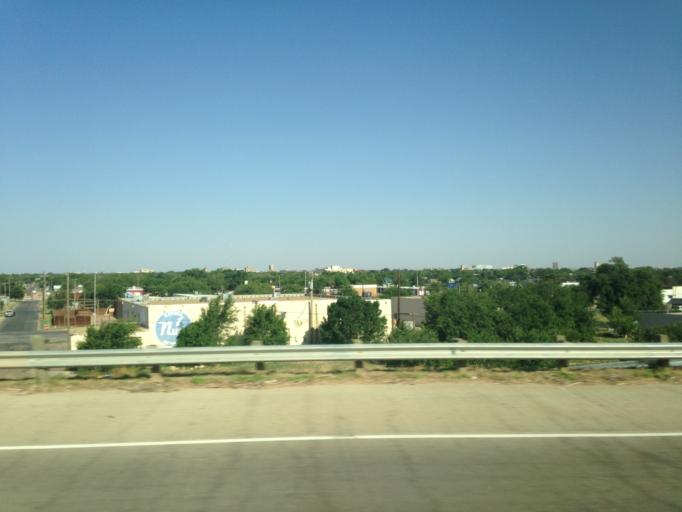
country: US
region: Texas
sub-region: Lubbock County
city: Lubbock
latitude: 33.5718
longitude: -101.8440
